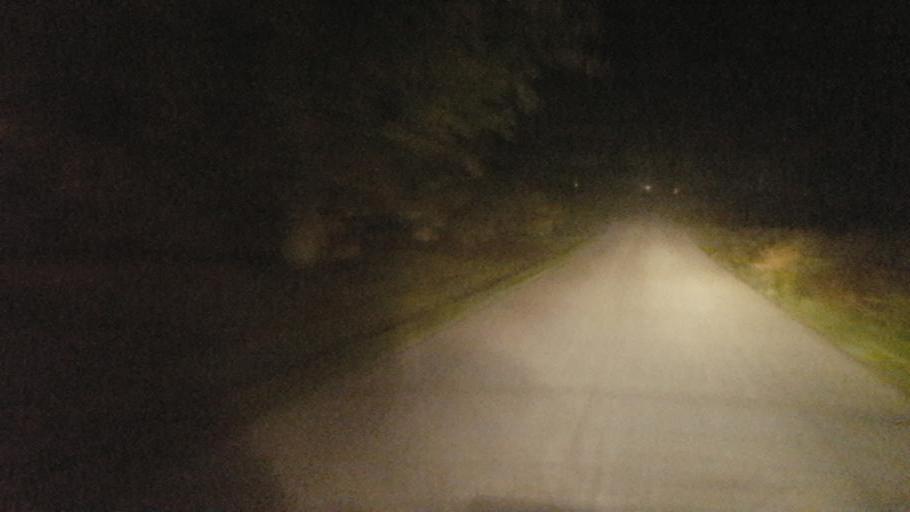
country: US
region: Ohio
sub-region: Knox County
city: Fredericktown
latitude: 40.5306
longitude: -82.5619
